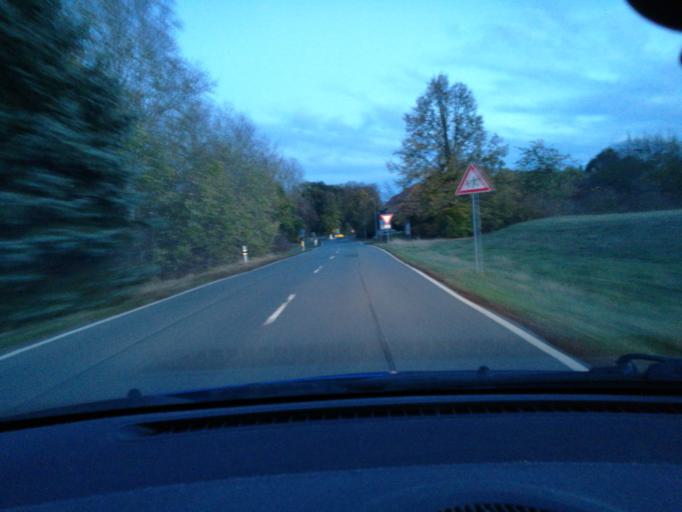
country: DE
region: Lower Saxony
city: Gartow
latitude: 53.0280
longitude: 11.4682
